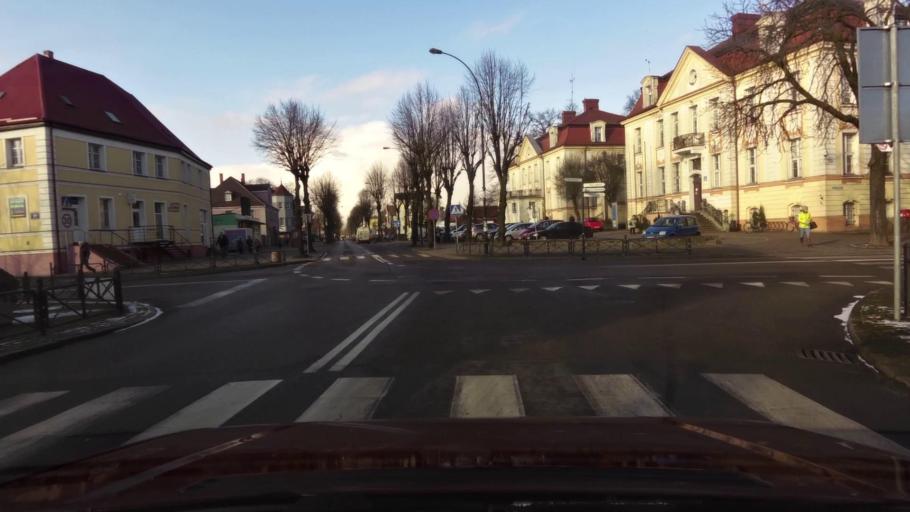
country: PL
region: West Pomeranian Voivodeship
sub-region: Powiat bialogardzki
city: Bialogard
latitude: 54.0078
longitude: 15.9859
